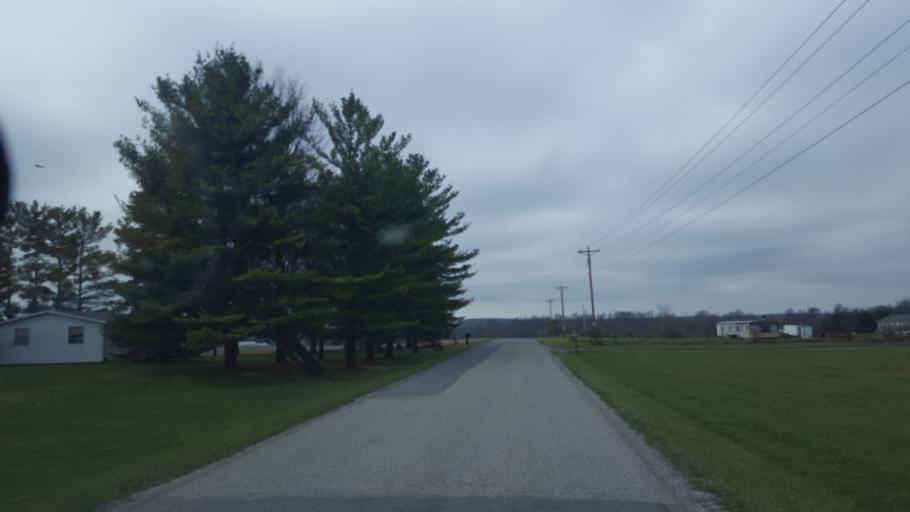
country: US
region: Ohio
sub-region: Knox County
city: Fredericktown
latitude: 40.4723
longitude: -82.6470
